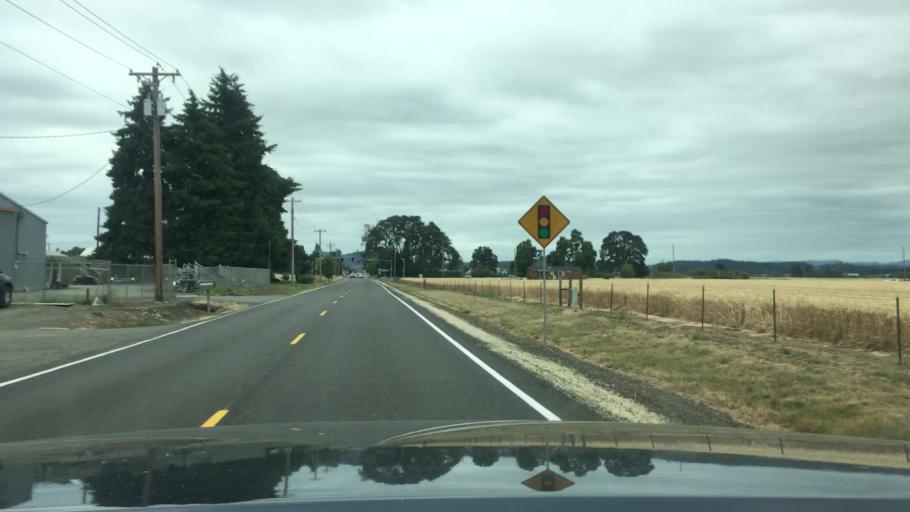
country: US
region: Oregon
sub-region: Lane County
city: Junction City
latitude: 44.1054
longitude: -123.2084
